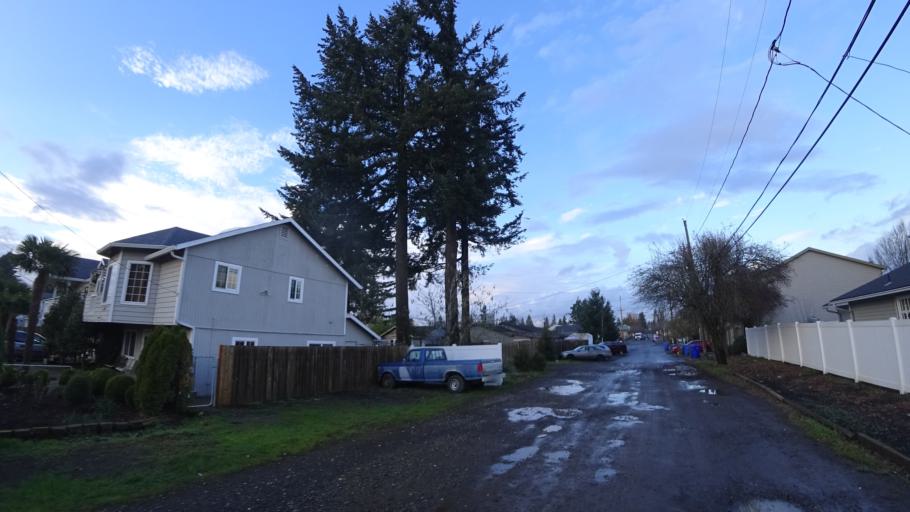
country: US
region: Oregon
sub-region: Multnomah County
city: Lents
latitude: 45.5177
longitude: -122.5403
